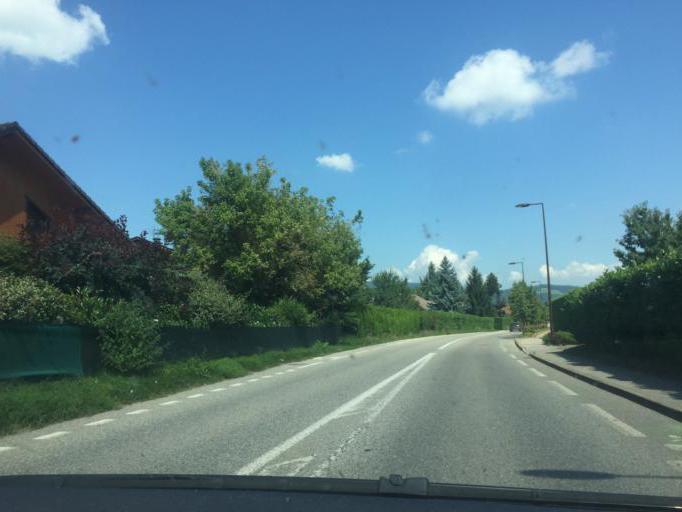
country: FR
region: Rhone-Alpes
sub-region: Departement de la Haute-Savoie
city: Poisy
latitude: 45.9139
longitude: 6.0531
